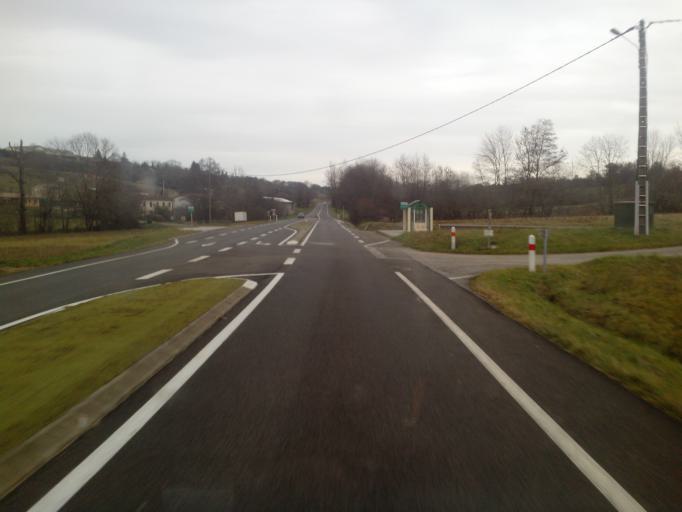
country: FR
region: Midi-Pyrenees
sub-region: Departement de l'Ariege
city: Foix
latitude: 43.0072
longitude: 1.4935
